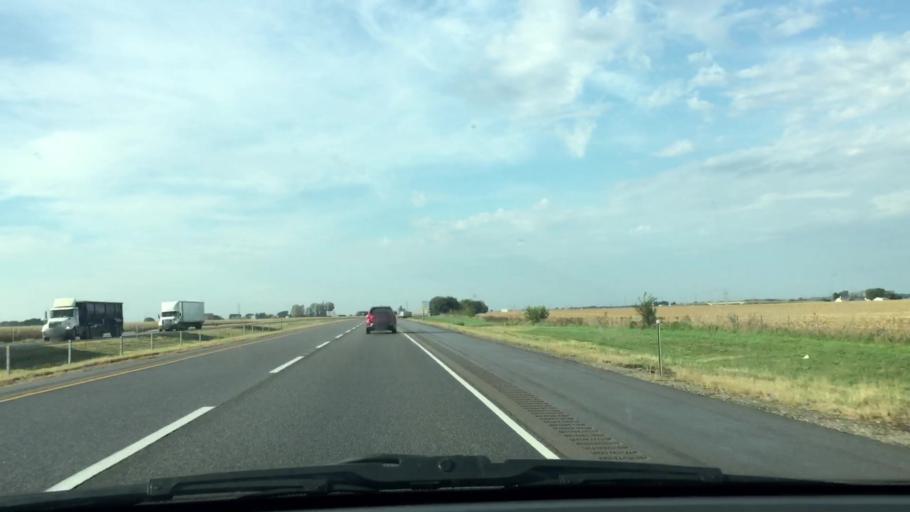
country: US
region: Illinois
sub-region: Lee County
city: Dixon
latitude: 41.7872
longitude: -89.5363
